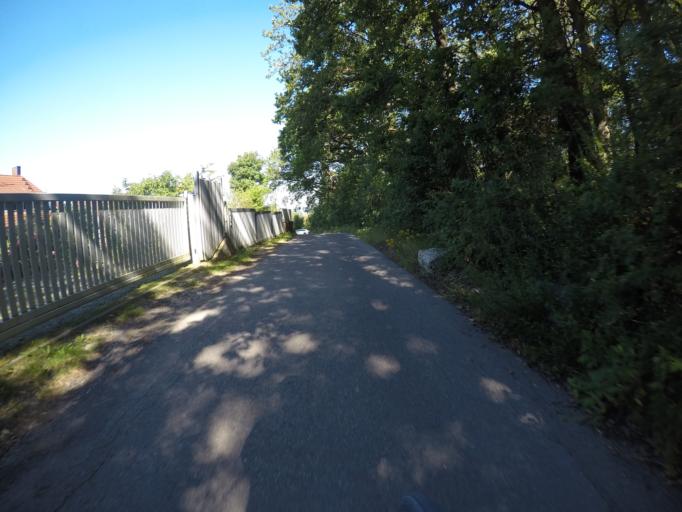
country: DE
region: Baden-Wuerttemberg
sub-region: Regierungsbezirk Stuttgart
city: Stuttgart-Ost
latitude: 48.7720
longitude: 9.2135
